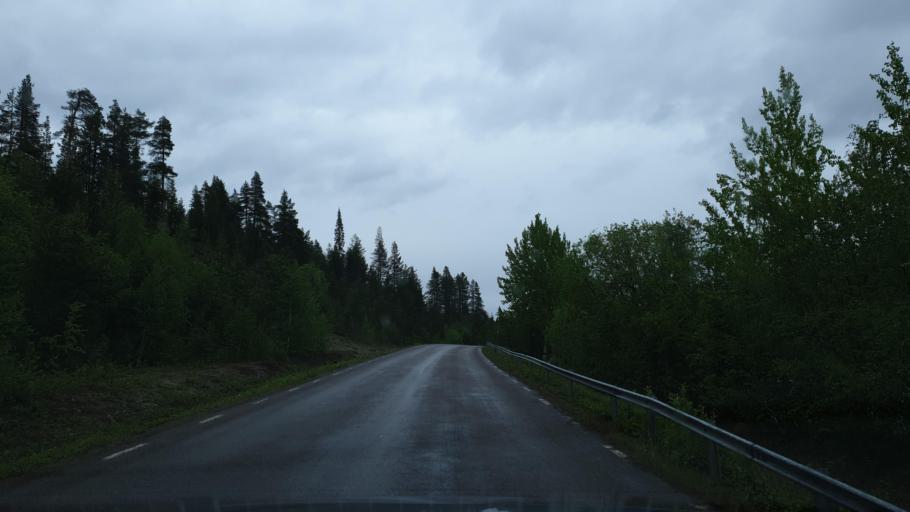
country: SE
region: Norrbotten
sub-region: Kiruna Kommun
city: Kiruna
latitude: 67.8891
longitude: 21.0257
